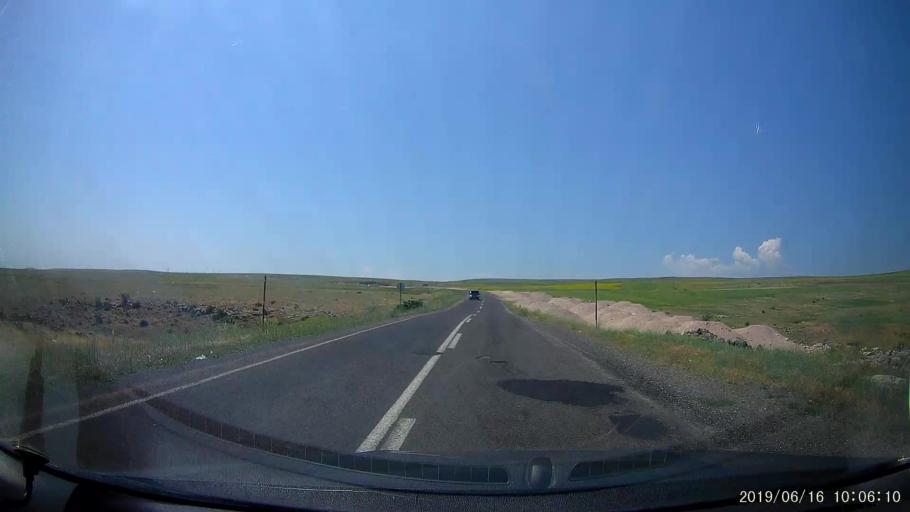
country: TR
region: Kars
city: Digor
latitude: 40.2590
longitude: 43.5411
